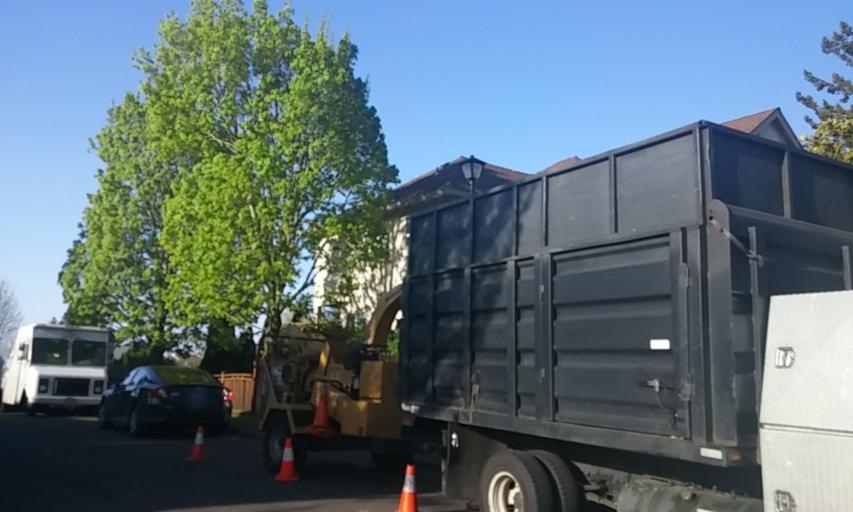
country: US
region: Oregon
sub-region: Washington County
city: Cedar Mill
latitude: 45.5432
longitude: -122.7898
